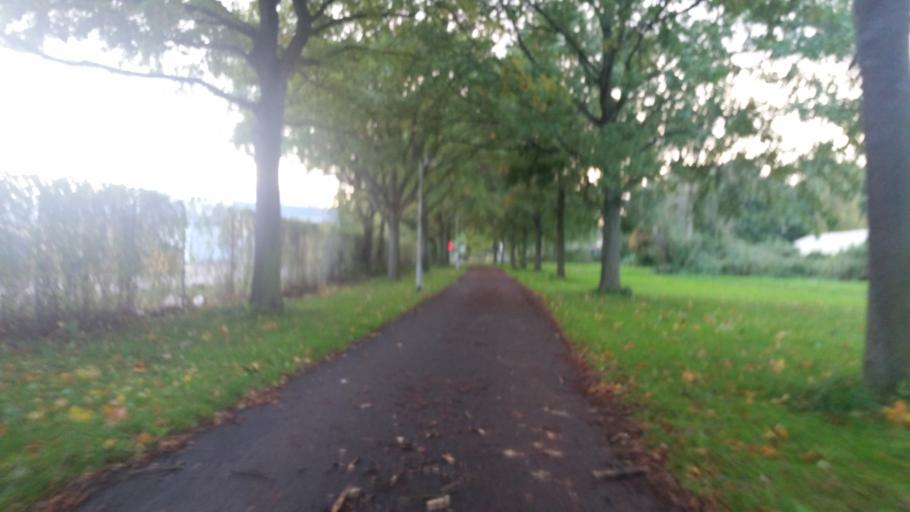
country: DE
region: Lower Saxony
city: Hannover
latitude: 52.4001
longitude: 9.7561
